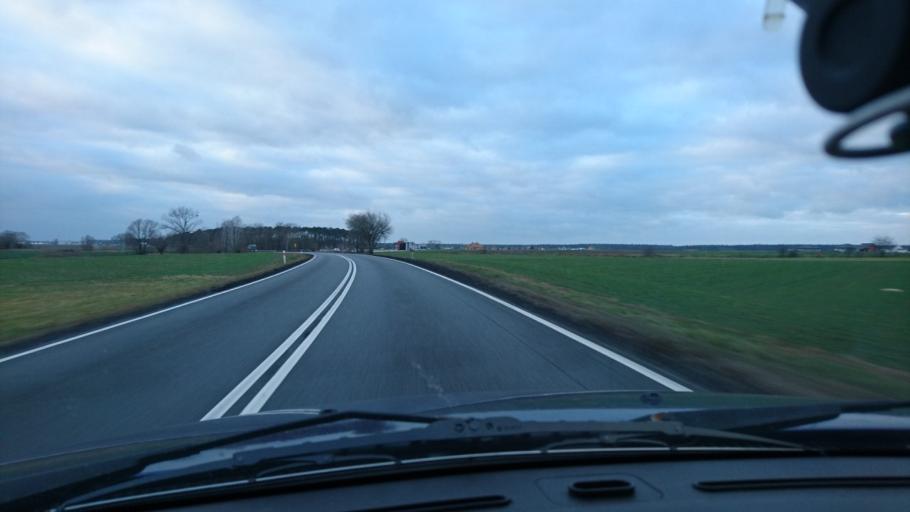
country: PL
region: Greater Poland Voivodeship
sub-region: Powiat kepinski
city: Opatow
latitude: 51.2199
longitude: 18.1361
